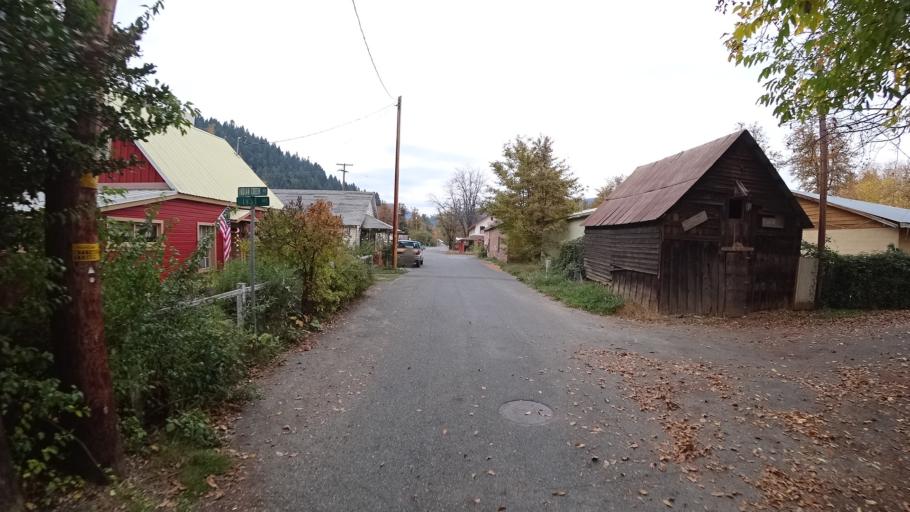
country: US
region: California
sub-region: Siskiyou County
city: Happy Camp
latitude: 41.7921
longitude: -123.3784
